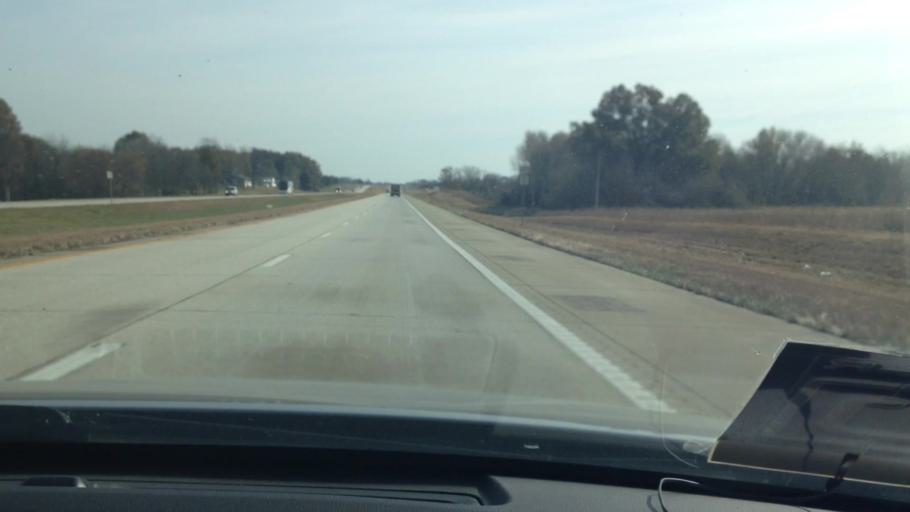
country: US
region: Missouri
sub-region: Henry County
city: Clinton
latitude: 38.4197
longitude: -93.8689
